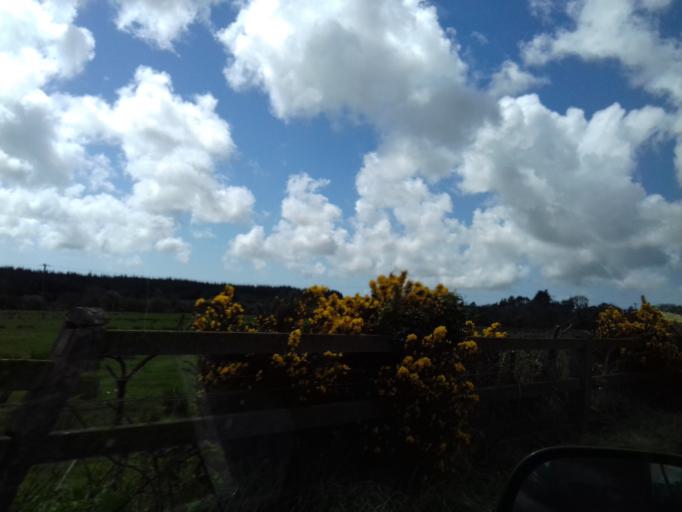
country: IE
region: Leinster
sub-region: Loch Garman
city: Loch Garman
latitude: 52.3076
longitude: -6.5513
